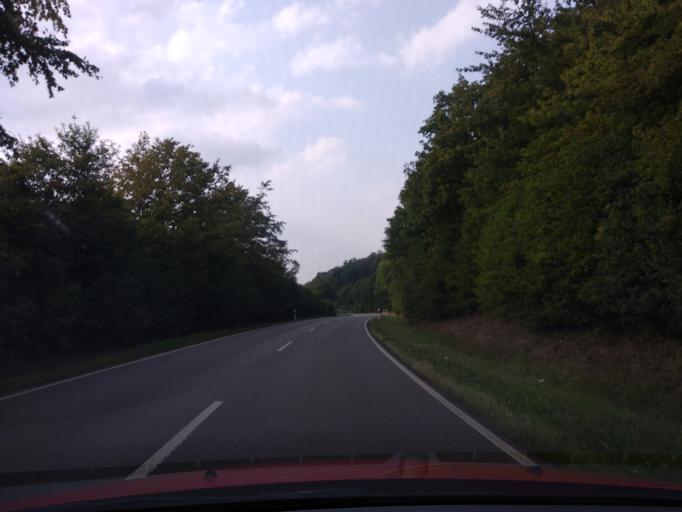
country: DE
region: Hesse
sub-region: Regierungsbezirk Kassel
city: Calden
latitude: 51.3793
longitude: 9.3707
